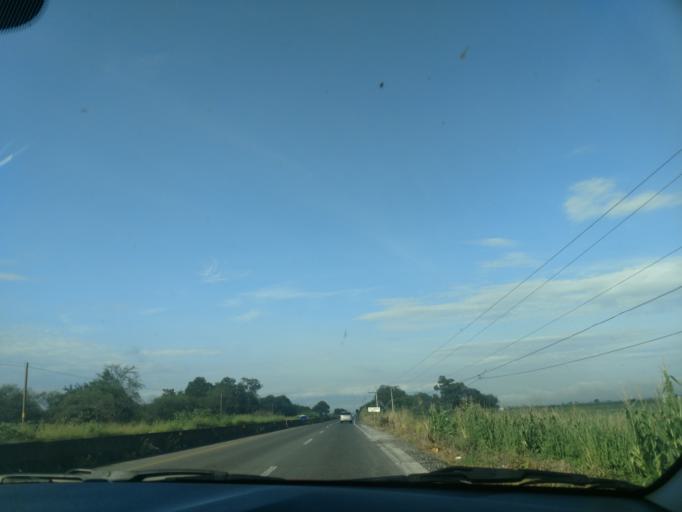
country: MX
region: Jalisco
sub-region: Ameca
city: Los Pocitos
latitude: 20.5516
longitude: -103.8965
